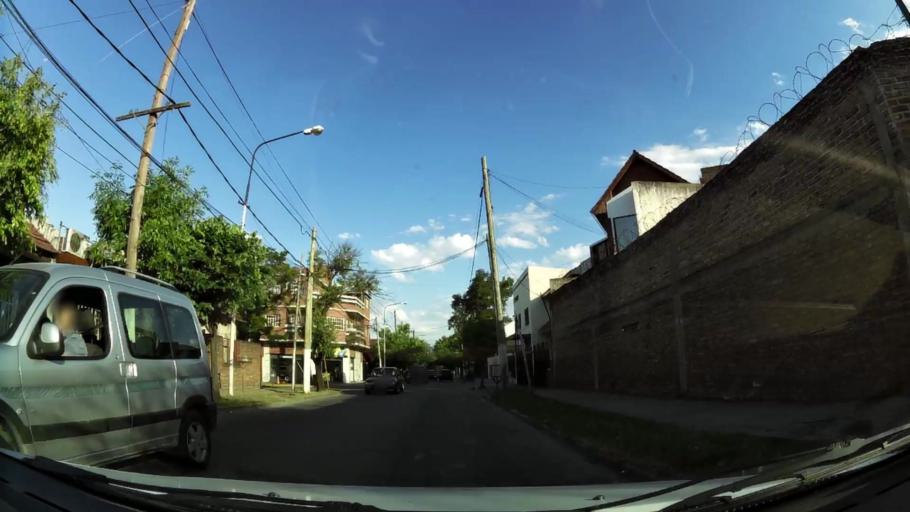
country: AR
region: Buenos Aires
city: Caseros
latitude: -34.5870
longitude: -58.5875
